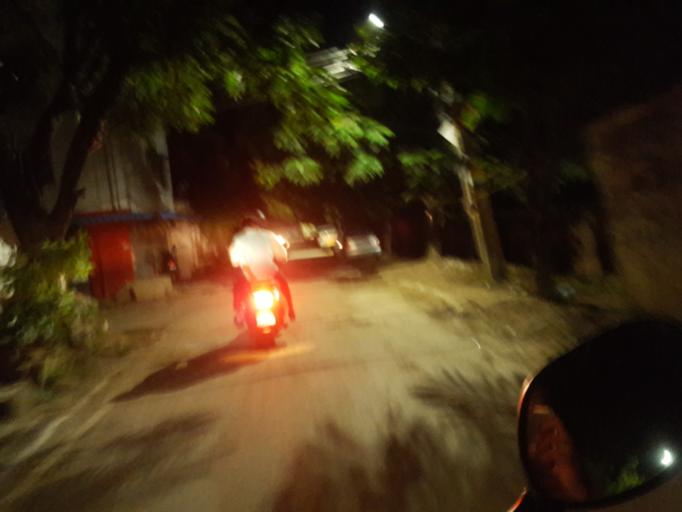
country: IN
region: Telangana
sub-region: Rangareddi
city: Kukatpalli
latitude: 17.4860
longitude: 78.3932
